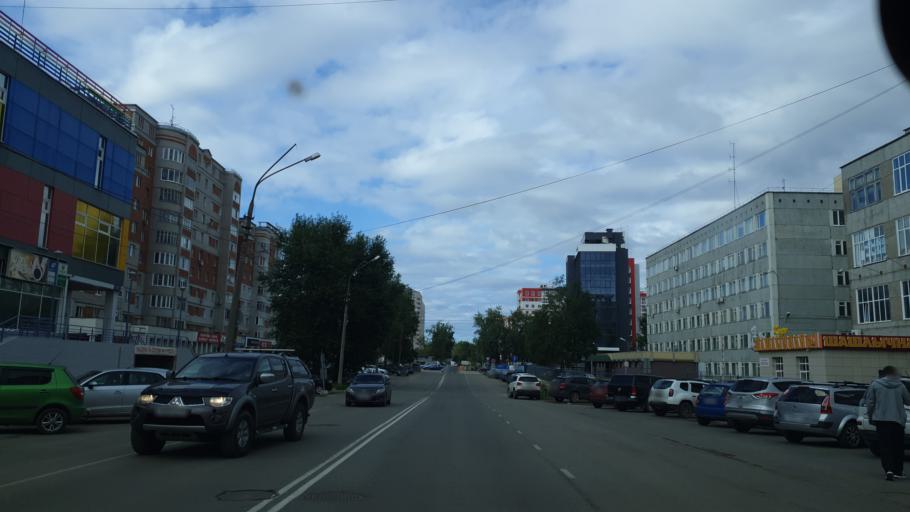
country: RU
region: Komi Republic
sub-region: Syktyvdinskiy Rayon
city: Syktyvkar
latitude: 61.6734
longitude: 50.8248
